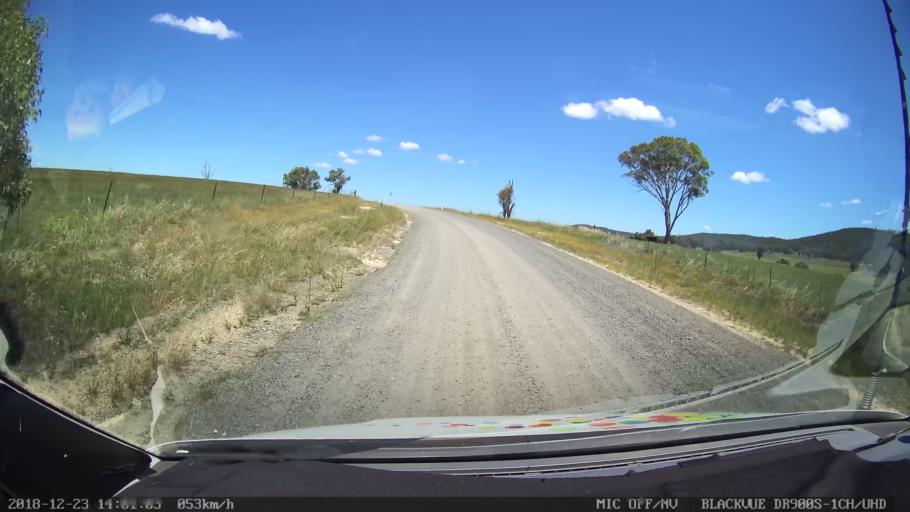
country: AU
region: New South Wales
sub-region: Tamworth Municipality
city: Manilla
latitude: -30.6186
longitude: 151.1088
